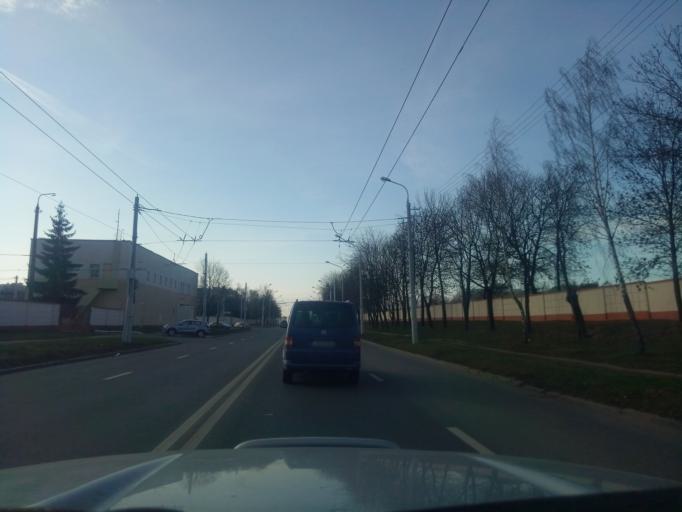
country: BY
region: Minsk
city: Novoye Medvezhino
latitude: 53.8834
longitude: 27.4887
